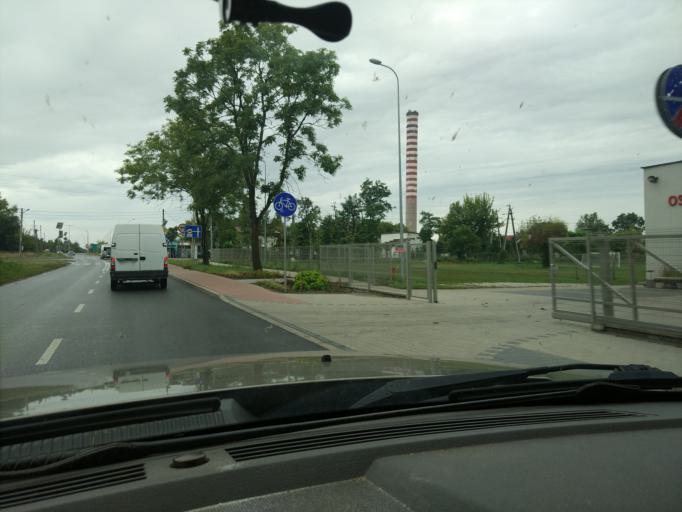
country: PL
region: Masovian Voivodeship
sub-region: Powiat pruszkowski
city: Brwinow
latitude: 52.1818
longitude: 20.7501
